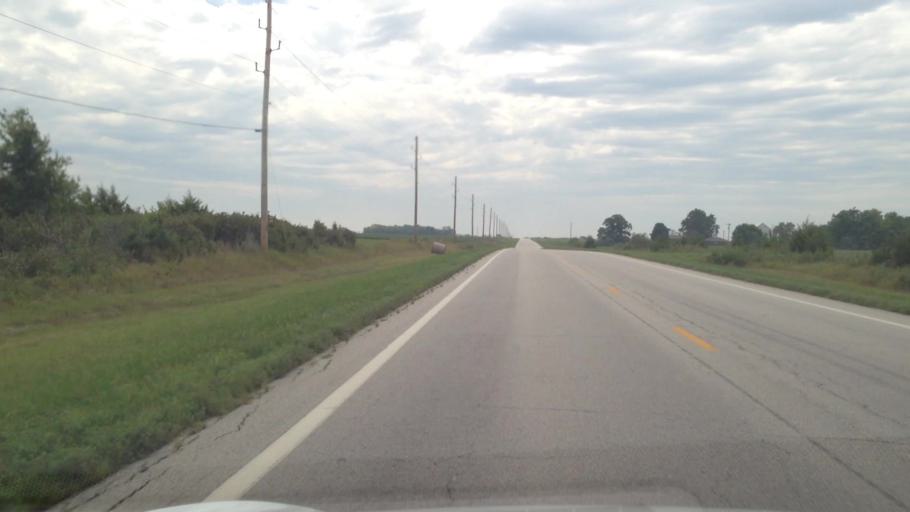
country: US
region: Kansas
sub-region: Allen County
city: Iola
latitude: 37.9440
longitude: -95.1700
